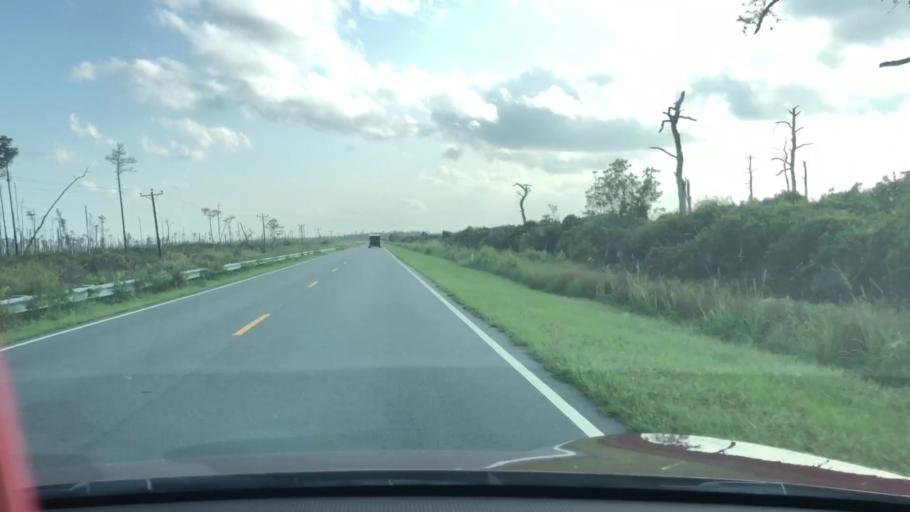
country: US
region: North Carolina
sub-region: Dare County
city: Wanchese
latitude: 35.6273
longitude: -75.7836
